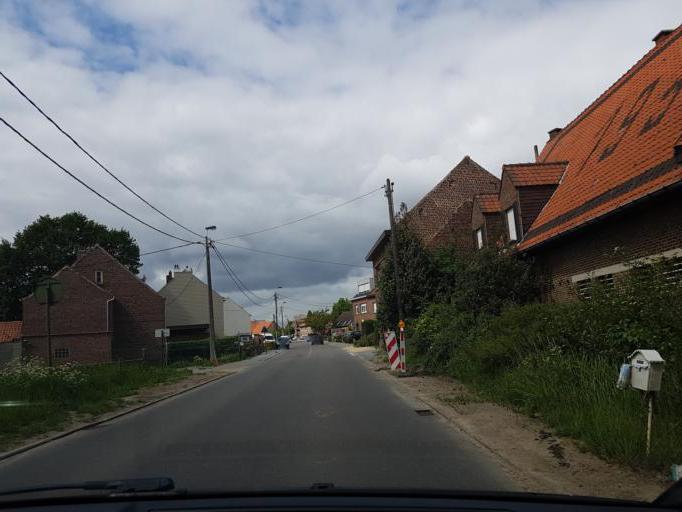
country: BE
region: Flanders
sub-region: Provincie Vlaams-Brabant
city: Grimbergen
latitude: 50.9378
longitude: 4.3892
